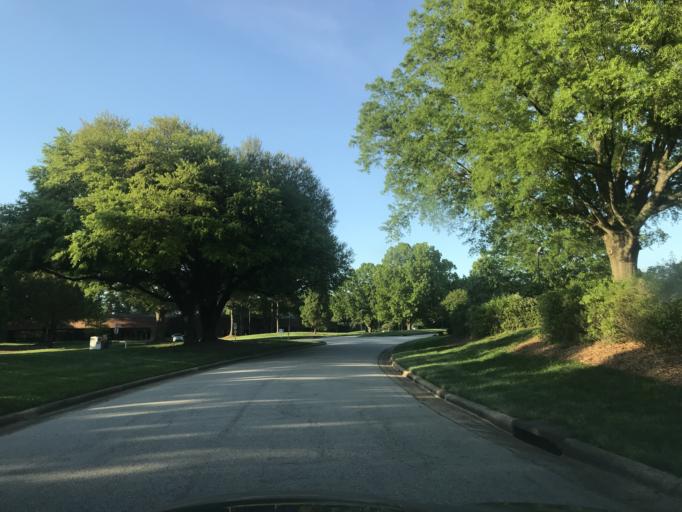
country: US
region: North Carolina
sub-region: Wake County
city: Raleigh
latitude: 35.8579
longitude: -78.5791
